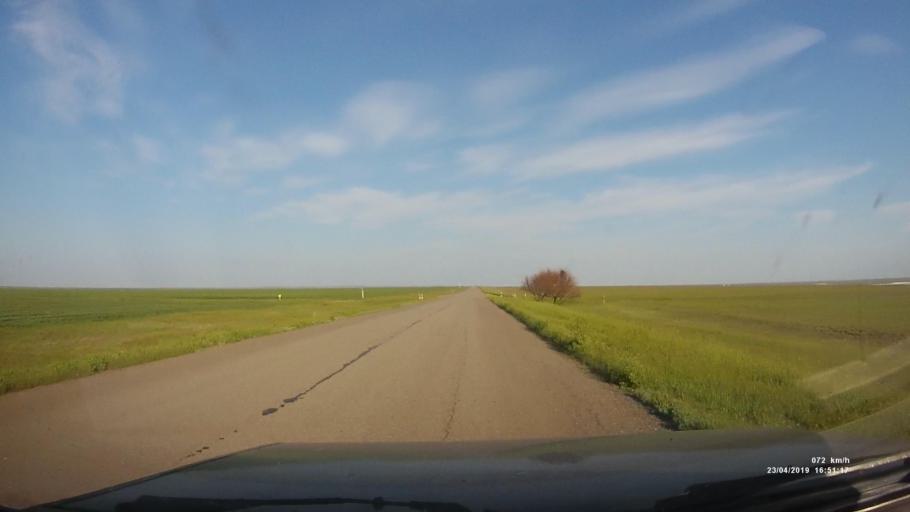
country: RU
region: Kalmykiya
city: Priyutnoye
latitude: 46.3237
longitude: 43.3037
